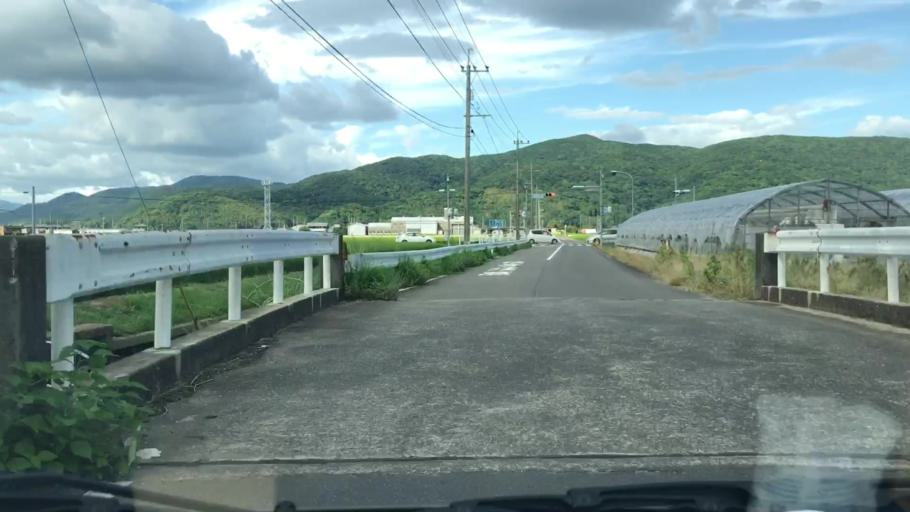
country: JP
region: Saga Prefecture
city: Kashima
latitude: 33.1189
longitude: 130.0702
